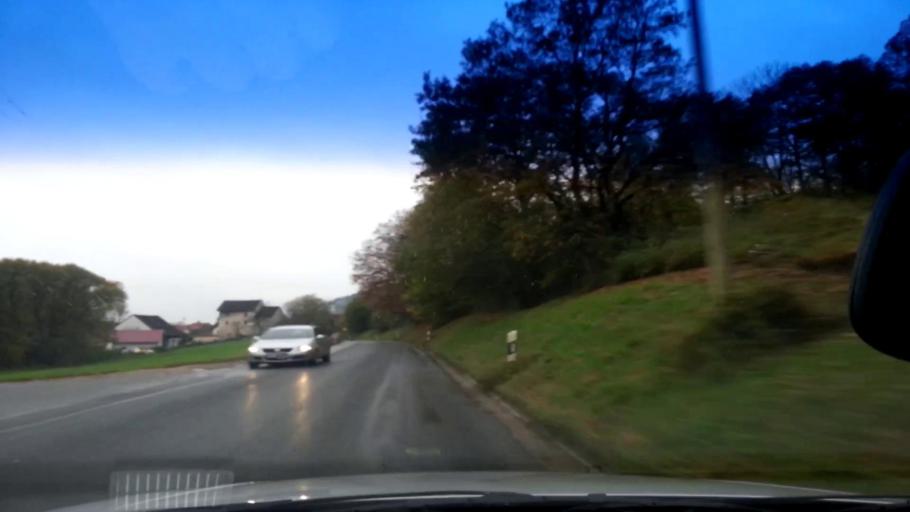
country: DE
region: Bavaria
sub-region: Upper Franconia
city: Wattendorf
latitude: 50.0140
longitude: 11.0770
